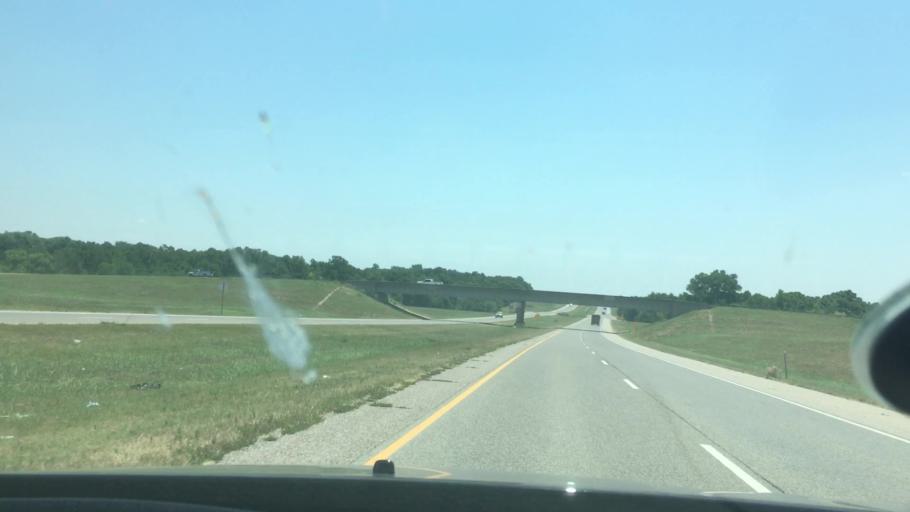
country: US
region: Oklahoma
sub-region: Pontotoc County
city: Ada
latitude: 34.7396
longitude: -96.6460
